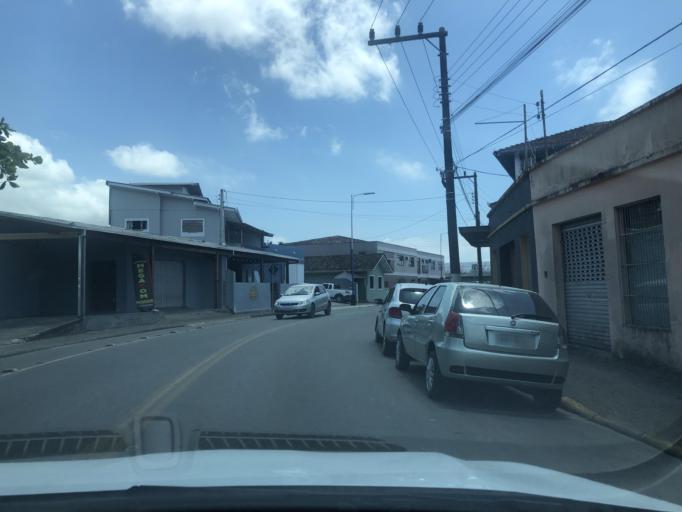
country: BR
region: Santa Catarina
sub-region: Sao Francisco Do Sul
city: Sao Francisco do Sul
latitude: -26.2498
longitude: -48.6405
